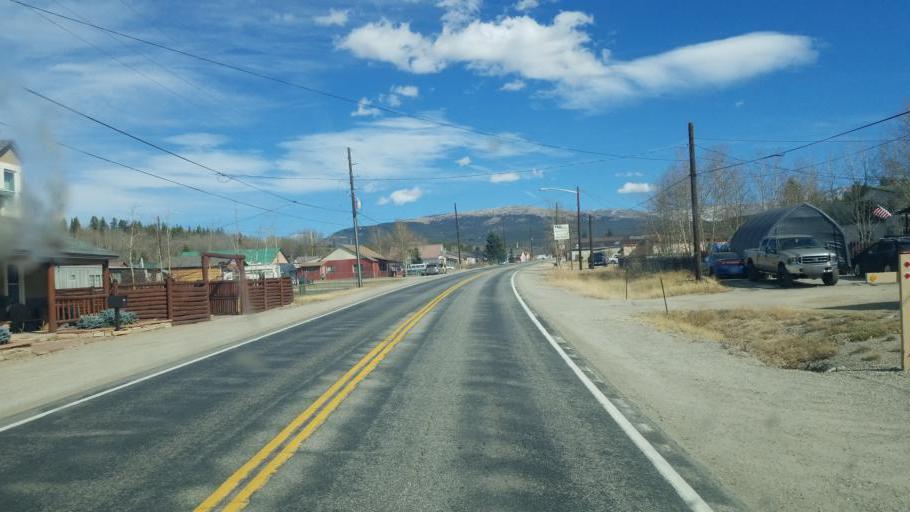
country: US
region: Colorado
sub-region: Lake County
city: Leadville North
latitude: 39.2358
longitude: -106.3157
